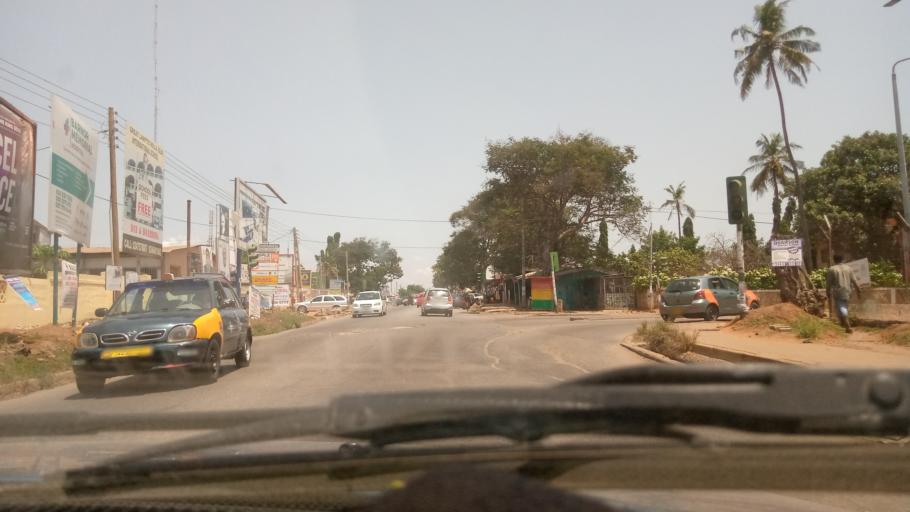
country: GH
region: Greater Accra
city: Accra
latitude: 5.5468
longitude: -0.2401
